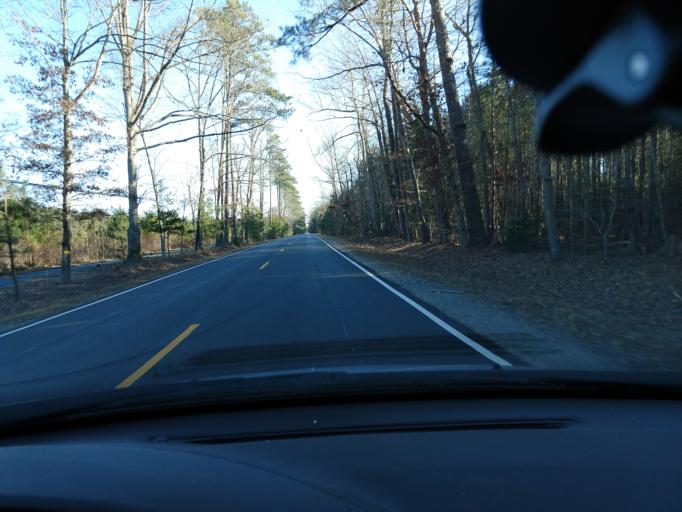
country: US
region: Virginia
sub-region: Surry County
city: Surry
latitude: 37.2766
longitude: -76.9107
